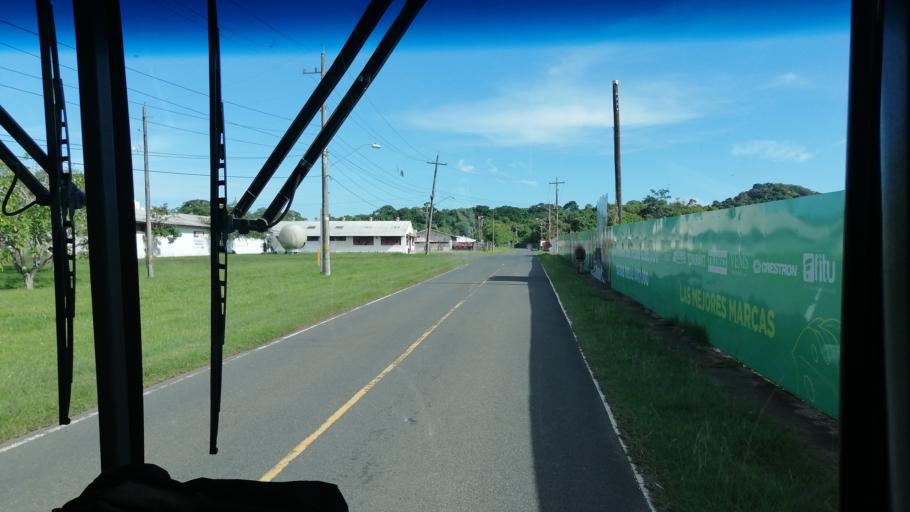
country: PA
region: Panama
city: Veracruz
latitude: 8.9035
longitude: -79.5879
